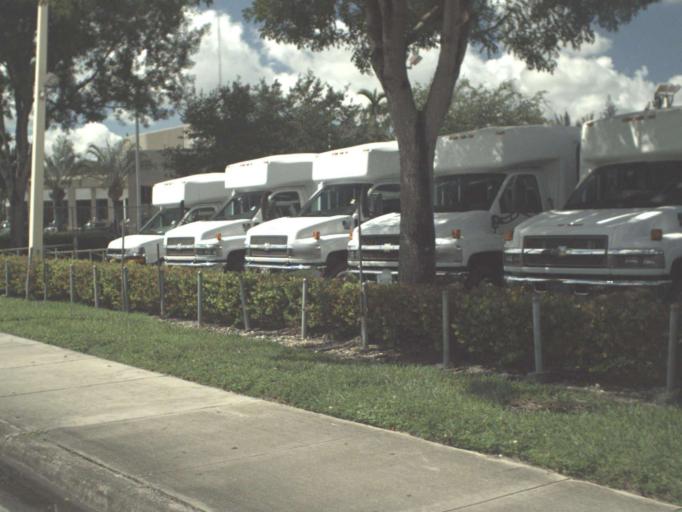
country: US
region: Florida
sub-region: Miami-Dade County
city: Andover
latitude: 25.9685
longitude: -80.2061
